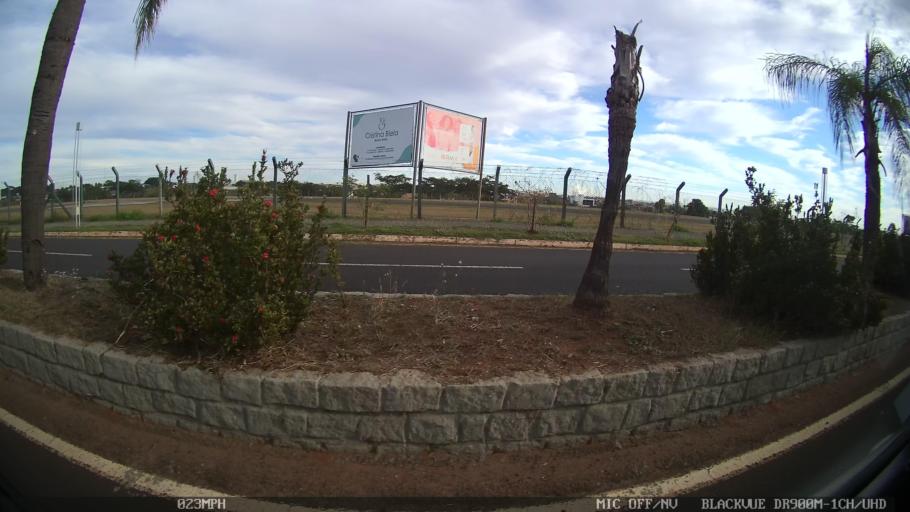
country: BR
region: Sao Paulo
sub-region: Catanduva
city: Catanduva
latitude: -21.1518
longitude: -48.9906
